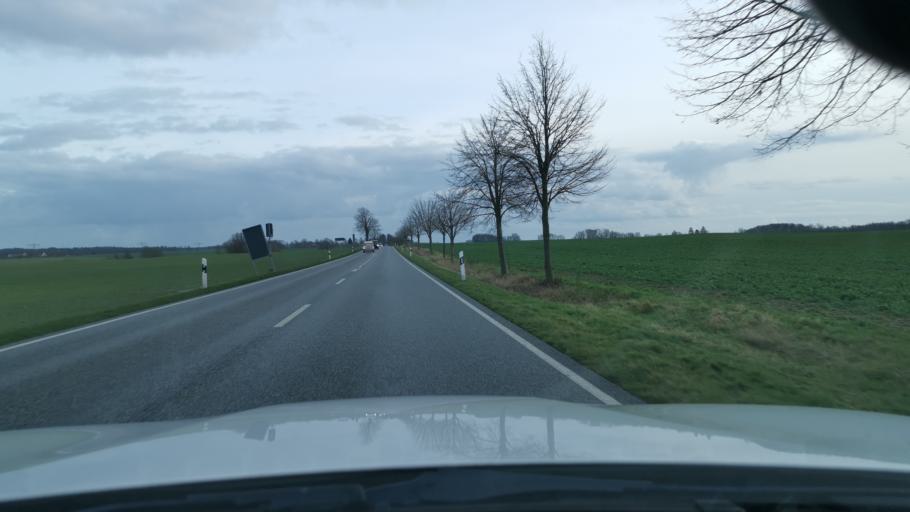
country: DE
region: Mecklenburg-Vorpommern
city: Dummerstorf
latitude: 53.9707
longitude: 12.2874
